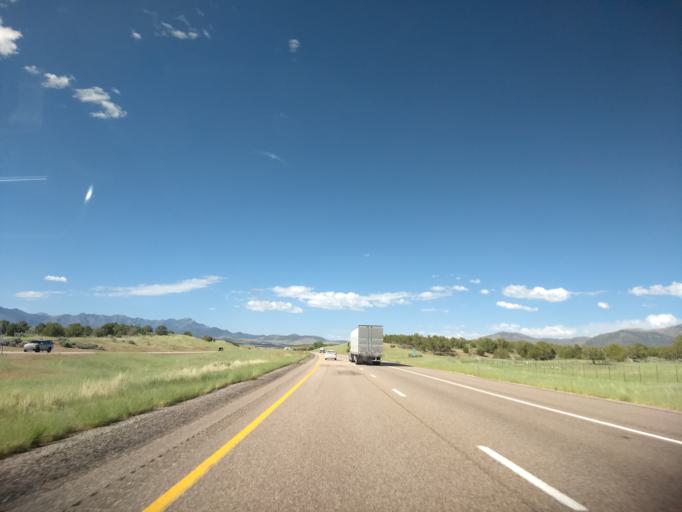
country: US
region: Utah
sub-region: Millard County
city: Fillmore
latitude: 39.0989
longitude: -112.2599
